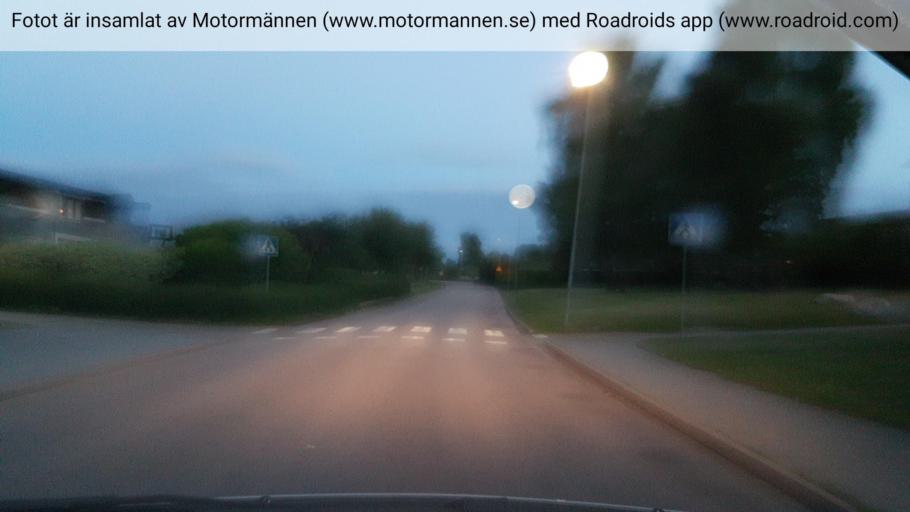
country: SE
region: Vaestmanland
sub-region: Vasteras
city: Vasteras
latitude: 59.6471
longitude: 16.5387
